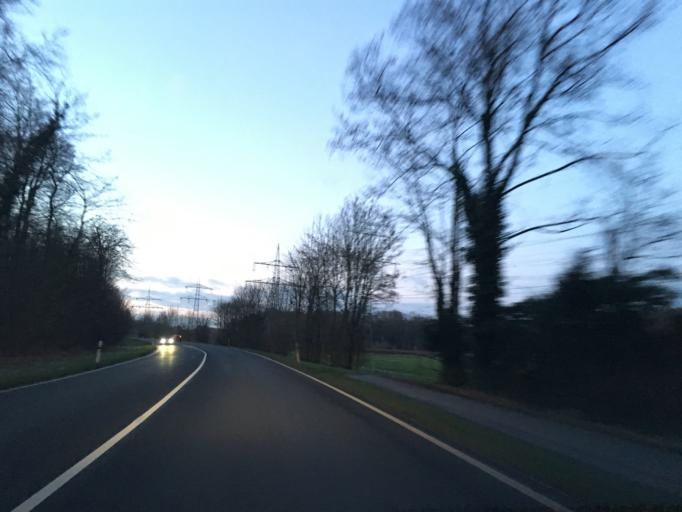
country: DE
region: North Rhine-Westphalia
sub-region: Regierungsbezirk Munster
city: Muenster
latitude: 51.8745
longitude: 7.6552
